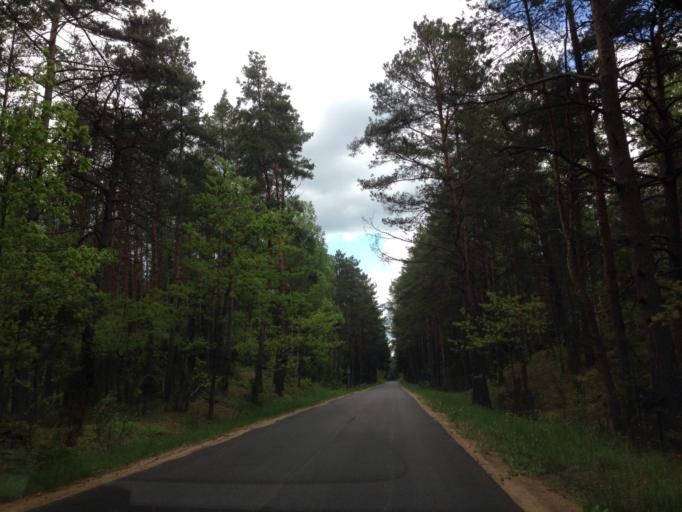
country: PL
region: Podlasie
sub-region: Powiat moniecki
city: Goniadz
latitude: 53.3531
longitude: 22.5983
